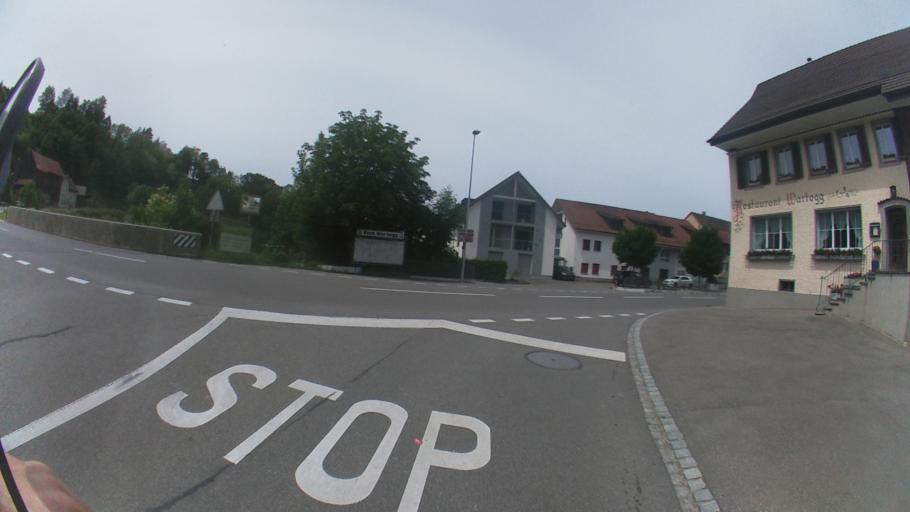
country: CH
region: Aargau
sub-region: Bezirk Zurzach
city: Tegerfelden
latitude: 47.5600
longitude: 8.2851
